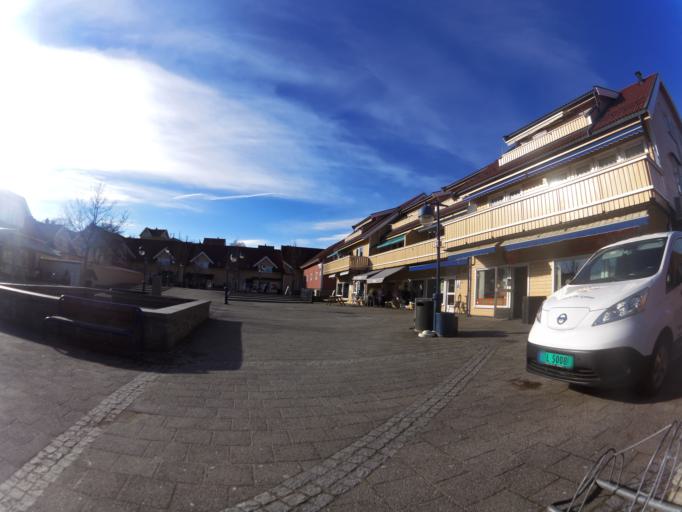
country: NO
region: Ostfold
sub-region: Fredrikstad
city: Fredrikstad
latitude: 59.2161
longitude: 10.9060
